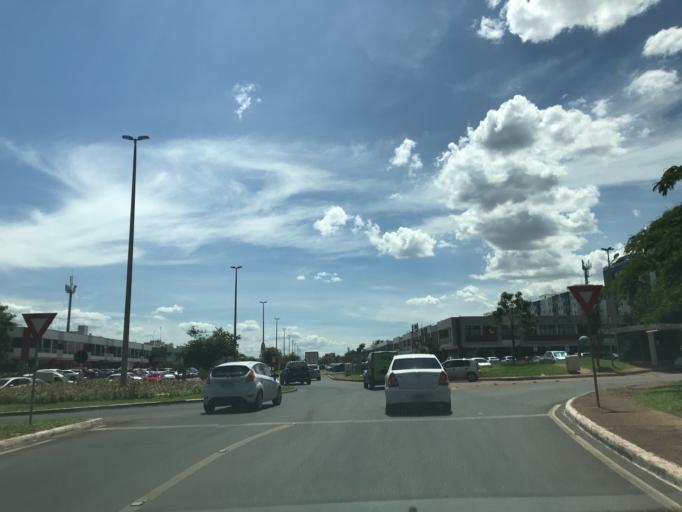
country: BR
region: Federal District
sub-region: Brasilia
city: Brasilia
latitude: -15.7985
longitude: -47.9214
